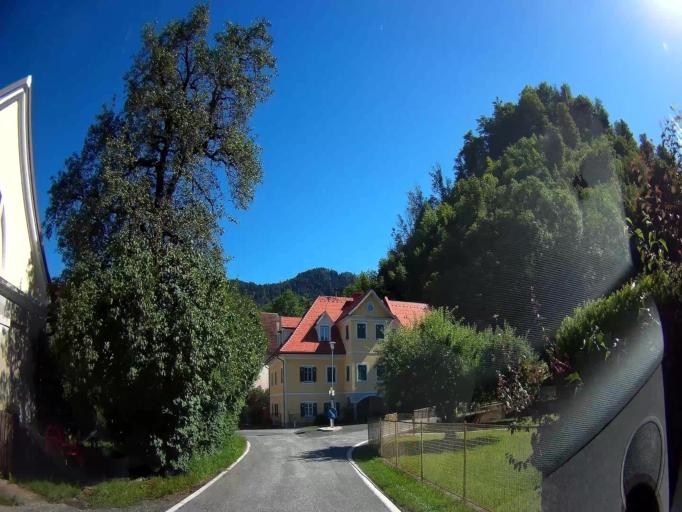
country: AT
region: Carinthia
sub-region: Politischer Bezirk Volkermarkt
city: Diex
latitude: 46.6982
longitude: 14.5837
